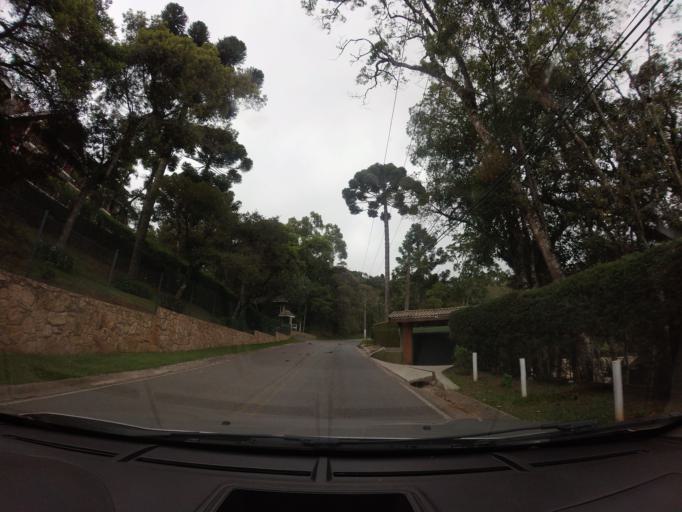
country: BR
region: Sao Paulo
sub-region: Campos Do Jordao
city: Campos do Jordao
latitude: -22.7207
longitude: -45.5801
